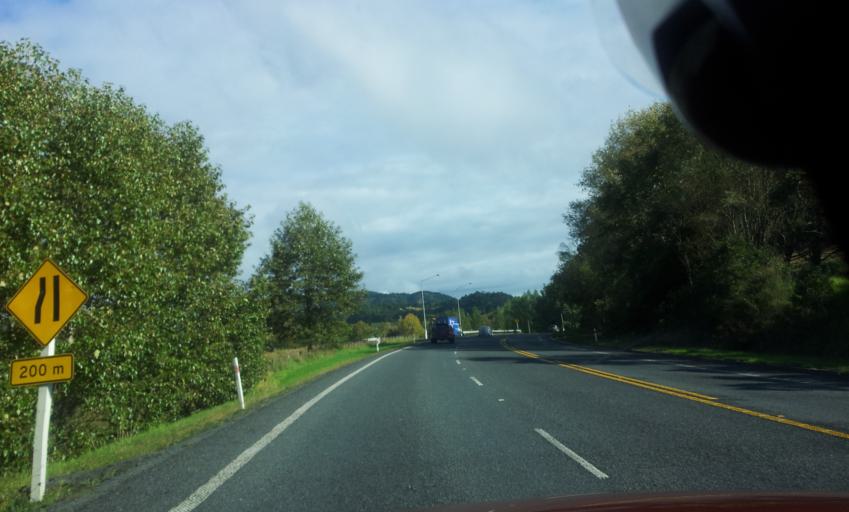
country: NZ
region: Auckland
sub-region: Auckland
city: Warkworth
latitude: -36.3885
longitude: 174.6439
